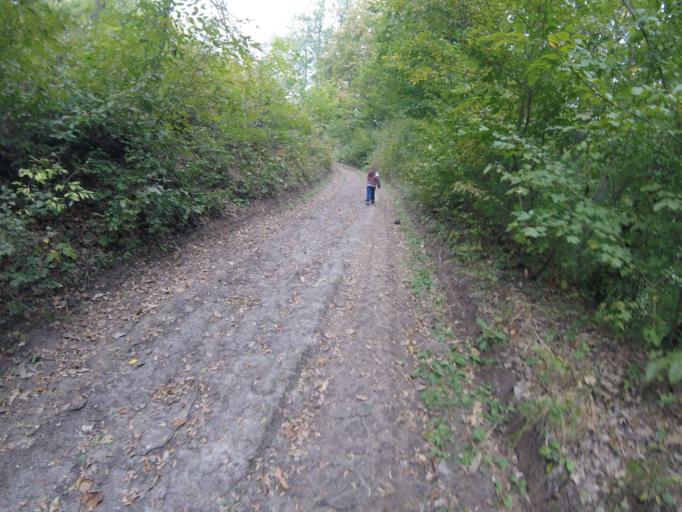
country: HU
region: Pest
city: Nagymaros
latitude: 47.8317
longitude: 18.9342
